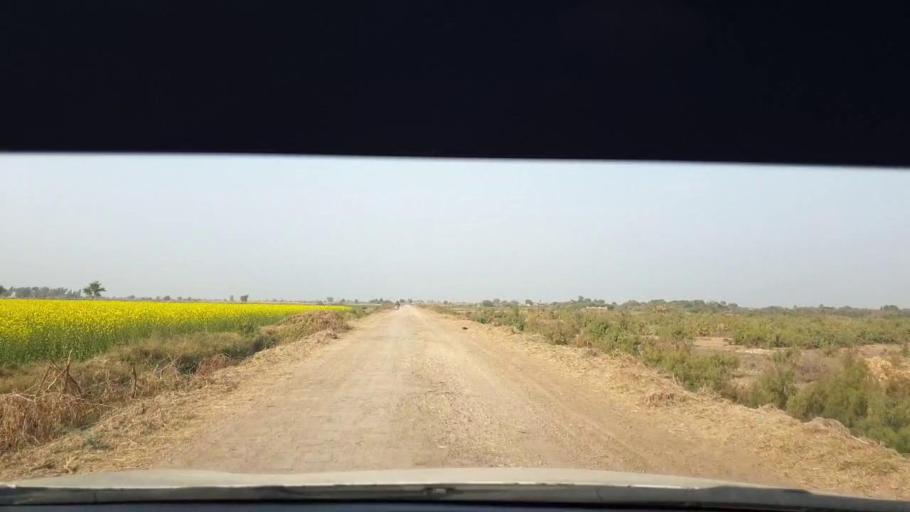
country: PK
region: Sindh
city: Berani
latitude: 25.7538
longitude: 68.9408
